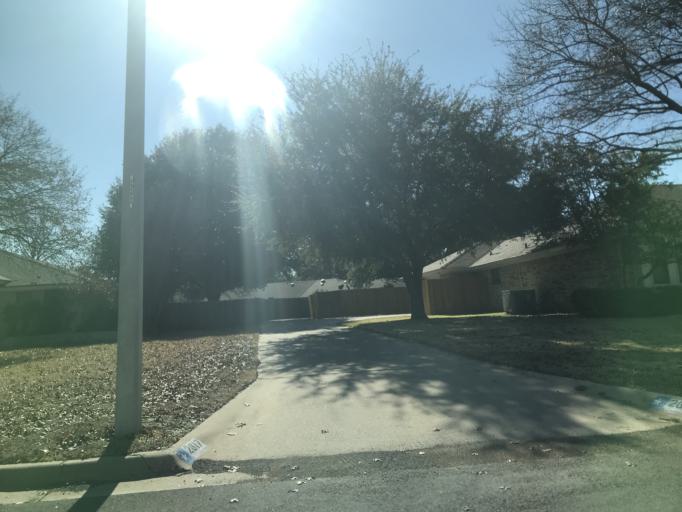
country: US
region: Texas
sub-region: Taylor County
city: Abilene
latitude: 32.3810
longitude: -99.7577
